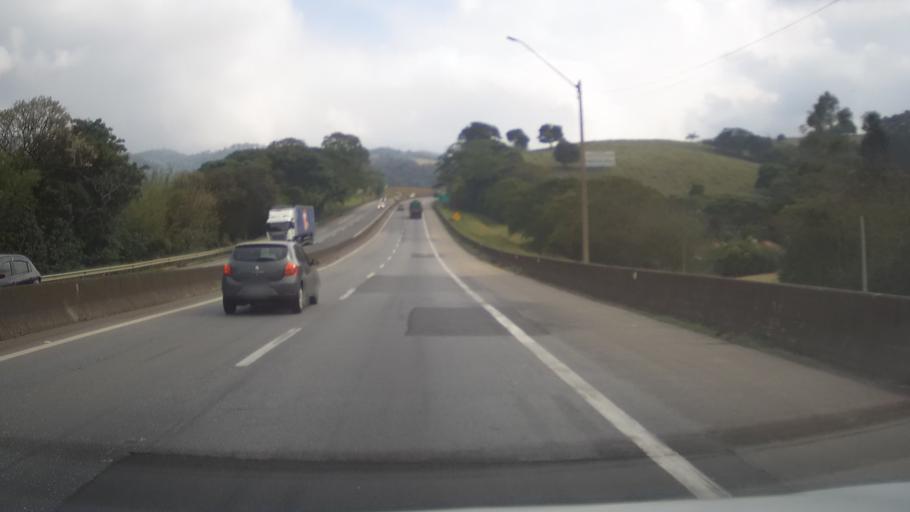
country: BR
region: Minas Gerais
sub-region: Extrema
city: Extrema
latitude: -22.8878
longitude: -46.4119
